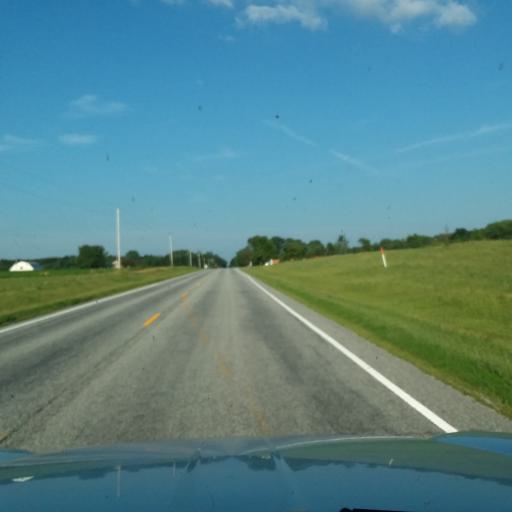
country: US
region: Indiana
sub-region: Johnson County
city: Franklin
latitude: 39.4117
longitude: -86.0236
